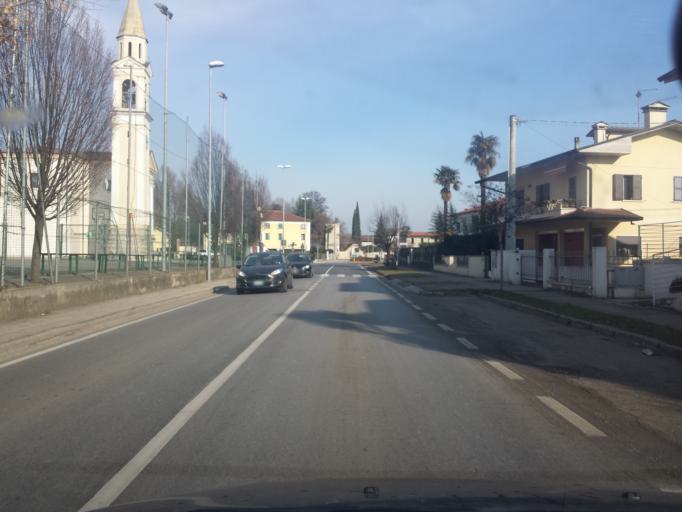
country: IT
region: Veneto
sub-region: Provincia di Vicenza
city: Bressanvido
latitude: 45.6475
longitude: 11.6346
